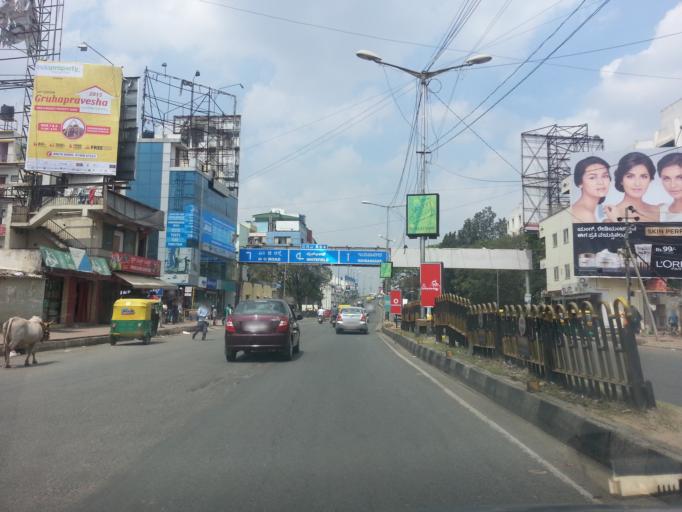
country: IN
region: Karnataka
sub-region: Bangalore Urban
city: Bangalore
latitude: 12.9578
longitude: 77.6413
